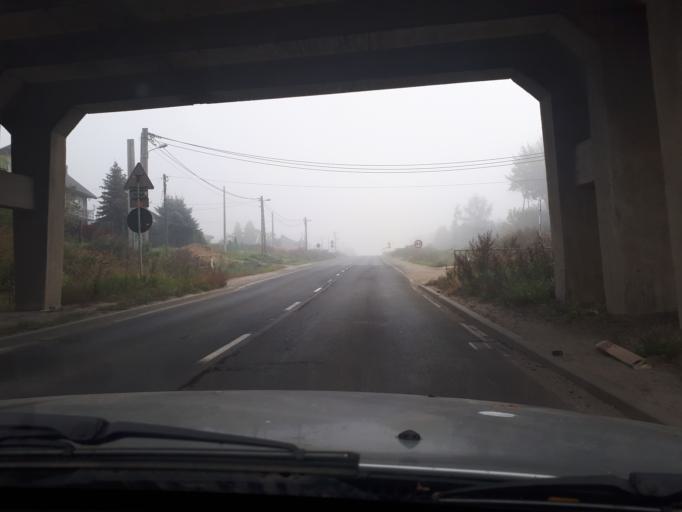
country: PL
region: Lesser Poland Voivodeship
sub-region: Powiat wielicki
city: Podleze
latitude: 50.0786
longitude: 20.1695
